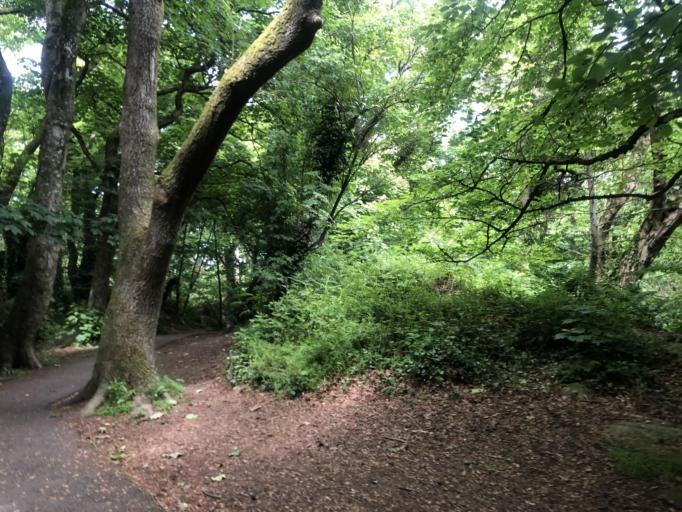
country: IE
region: Leinster
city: Dalkey
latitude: 53.2671
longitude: -6.1103
